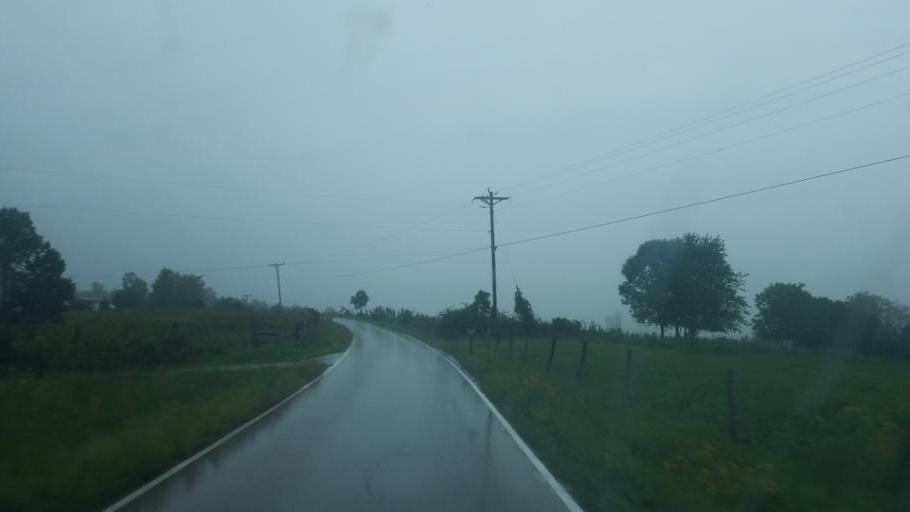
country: US
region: Kentucky
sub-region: Lewis County
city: Vanceburg
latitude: 38.4857
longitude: -83.5085
